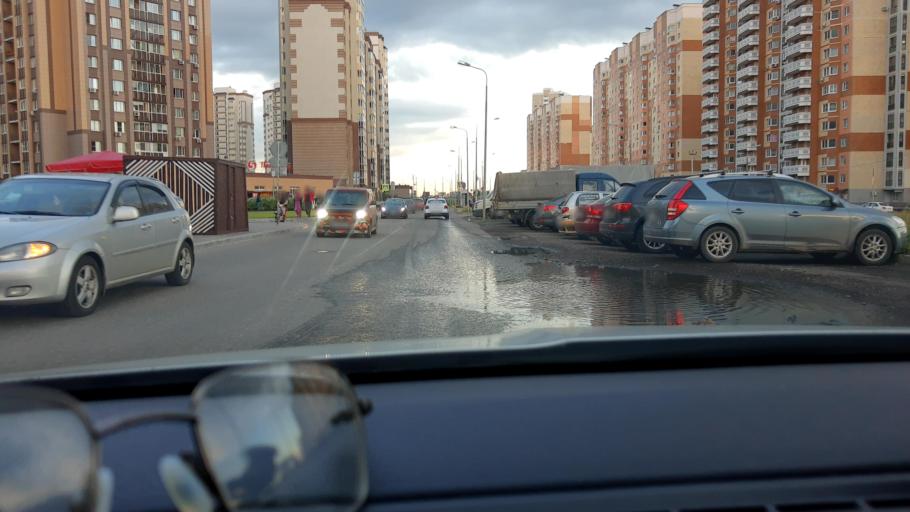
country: RU
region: Moskovskaya
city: Vostryakovo
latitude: 55.3998
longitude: 37.7696
